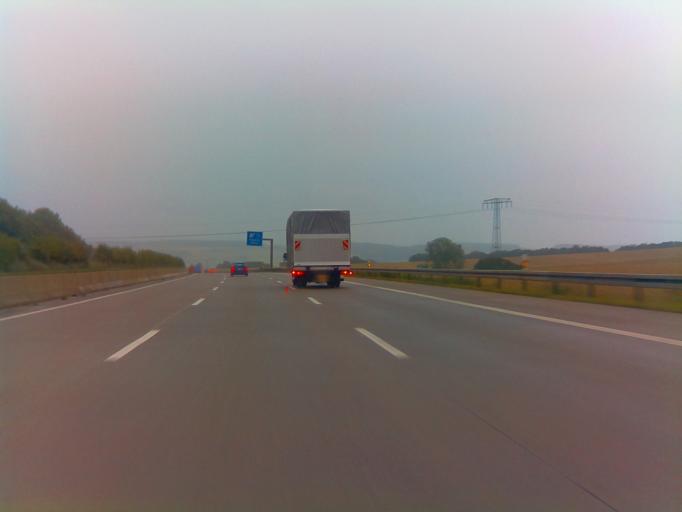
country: DE
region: Thuringia
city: Magdala
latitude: 50.9066
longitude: 11.4213
